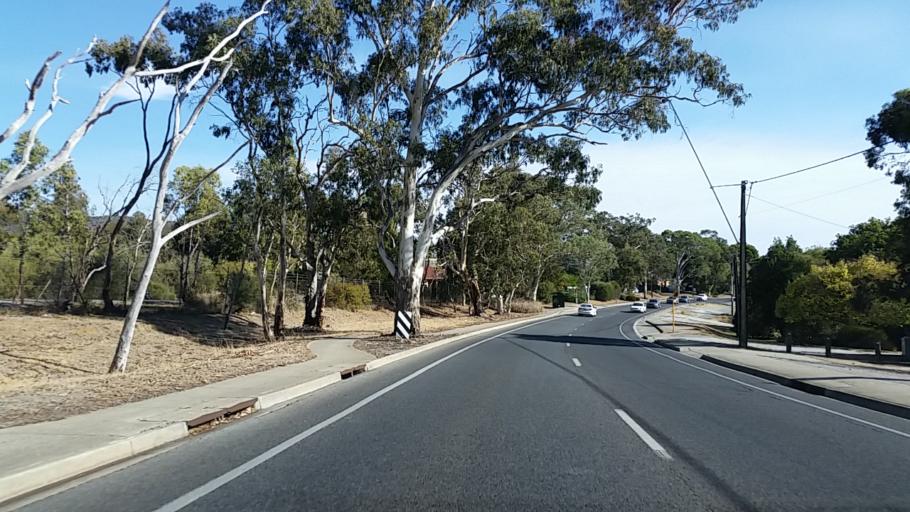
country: AU
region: South Australia
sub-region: Tea Tree Gully
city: Hope Valley
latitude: -34.8479
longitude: 138.7165
